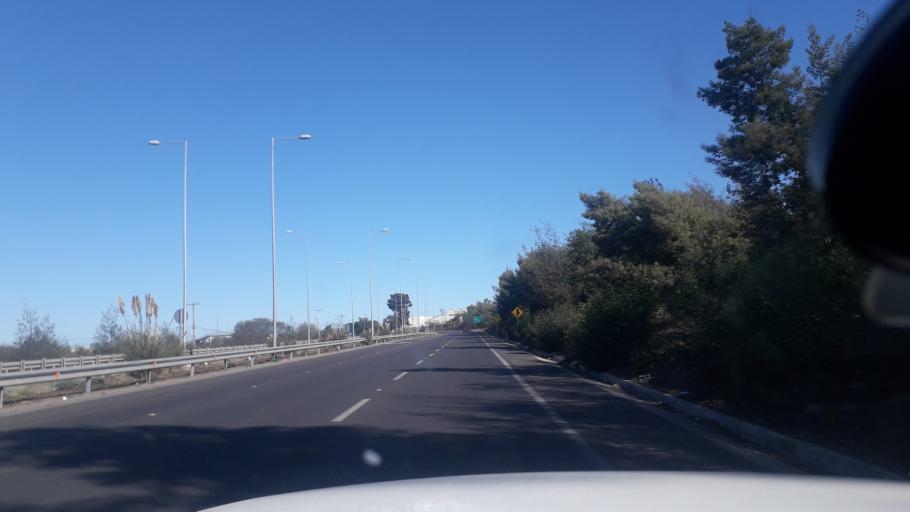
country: CL
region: Valparaiso
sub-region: Provincia de Valparaiso
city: Vina del Mar
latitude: -32.9550
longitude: -71.5096
